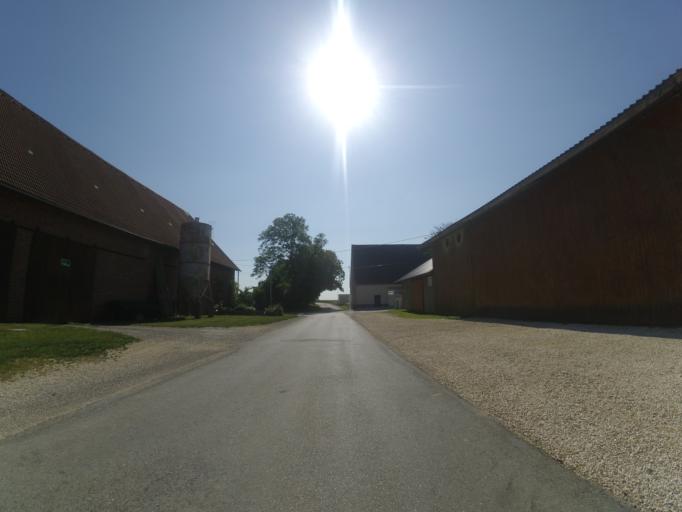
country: DE
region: Baden-Wuerttemberg
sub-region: Tuebingen Region
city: Beimerstetten
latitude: 48.4691
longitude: 9.9919
